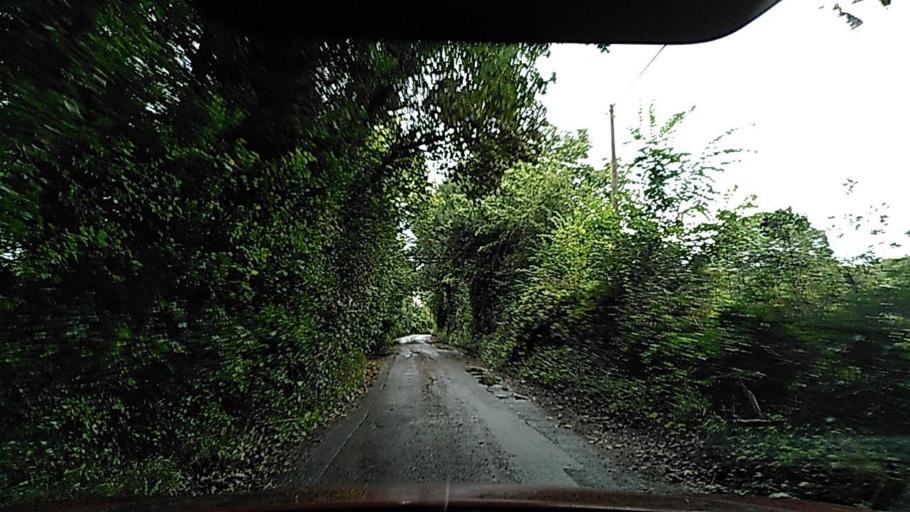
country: GB
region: England
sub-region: Oxfordshire
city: Sonning Common
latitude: 51.5096
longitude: -0.9940
